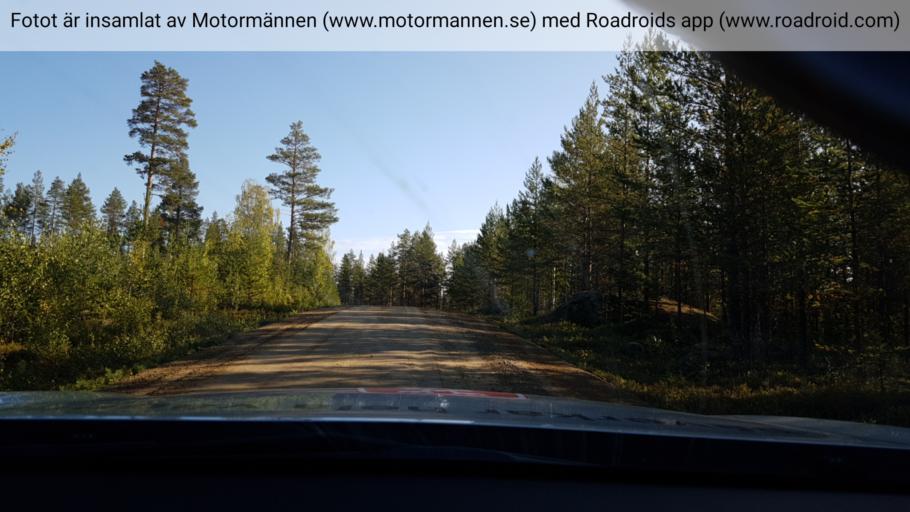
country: SE
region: Vaesterbotten
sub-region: Norsjo Kommun
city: Norsjoe
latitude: 64.5993
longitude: 19.3726
